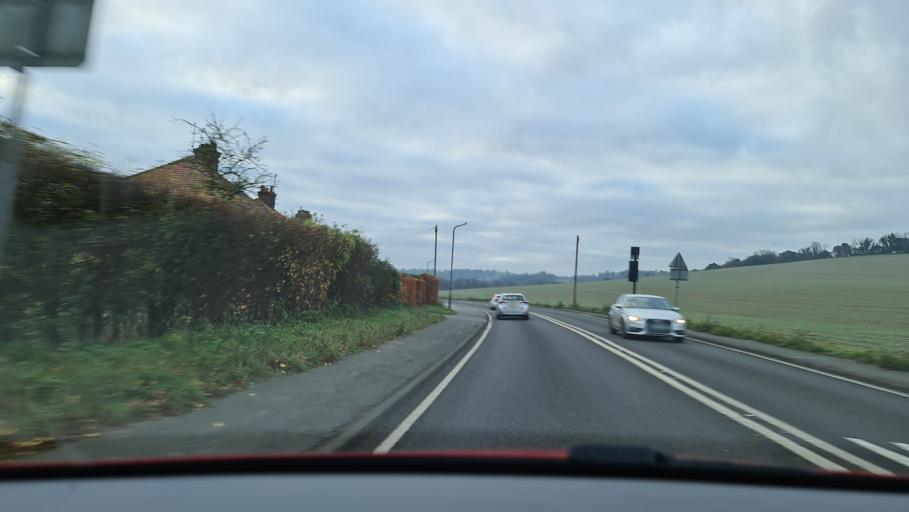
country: GB
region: England
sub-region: Buckinghamshire
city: High Wycombe
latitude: 51.6534
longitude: -0.8002
